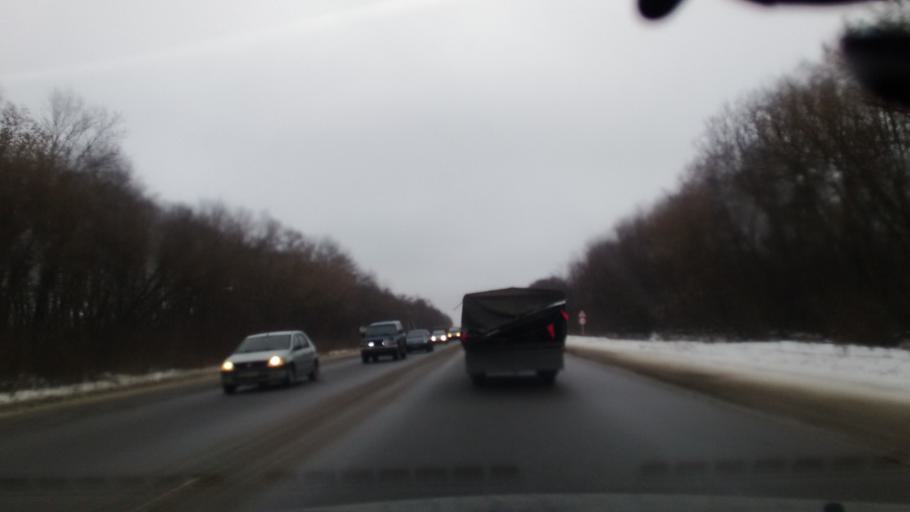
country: RU
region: Tula
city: Tula
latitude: 54.1423
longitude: 37.6604
